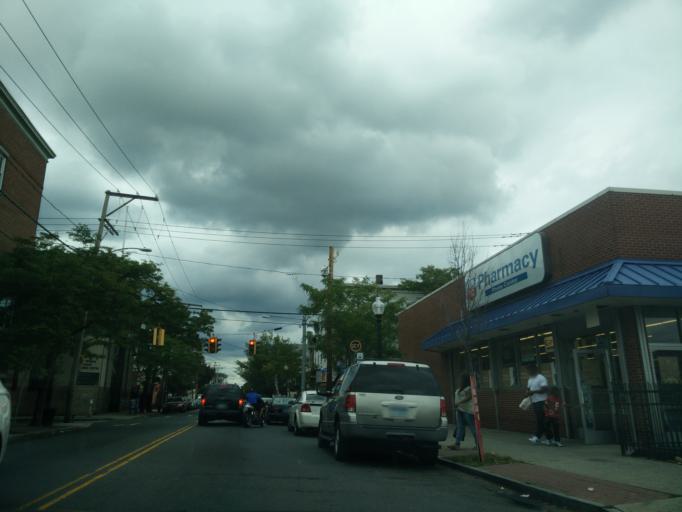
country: US
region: Connecticut
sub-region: Fairfield County
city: Bridgeport
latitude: 41.1888
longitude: -73.1806
